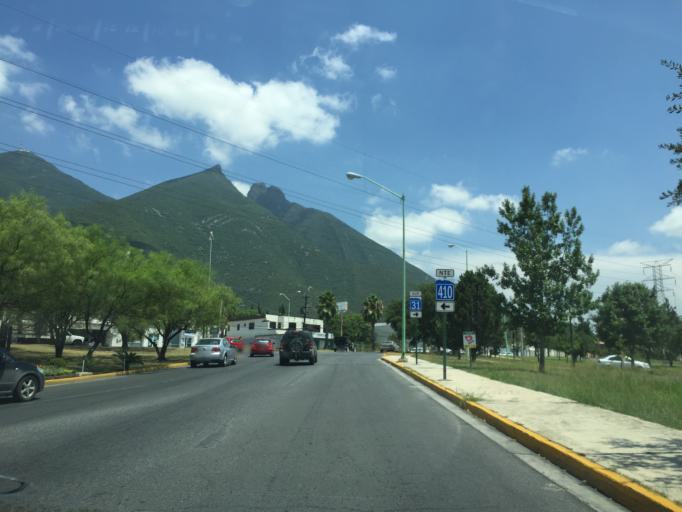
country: MX
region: Nuevo Leon
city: Guadalupe
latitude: 25.6469
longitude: -100.2686
